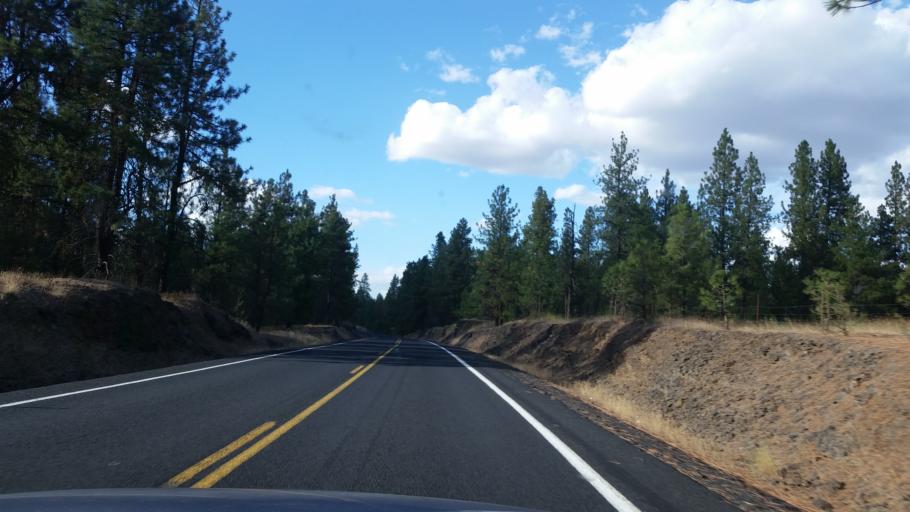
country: US
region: Washington
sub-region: Spokane County
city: Cheney
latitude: 47.4479
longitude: -117.5755
